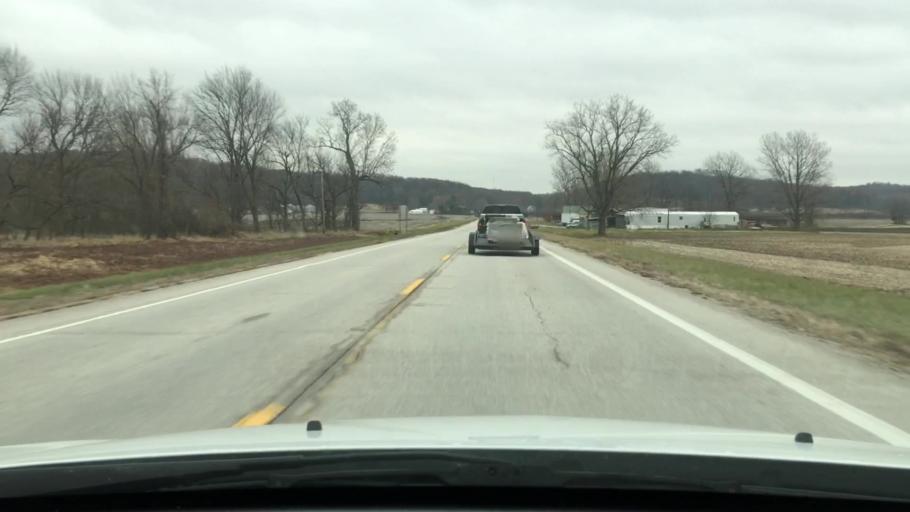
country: US
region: Missouri
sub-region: Pike County
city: Louisiana
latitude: 39.5081
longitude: -90.9803
